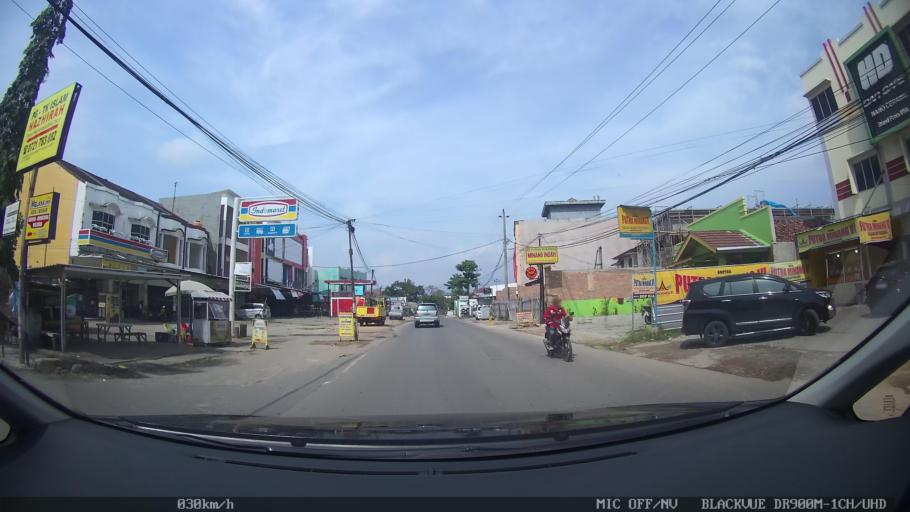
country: ID
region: Lampung
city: Kedaton
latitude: -5.3912
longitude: 105.2860
